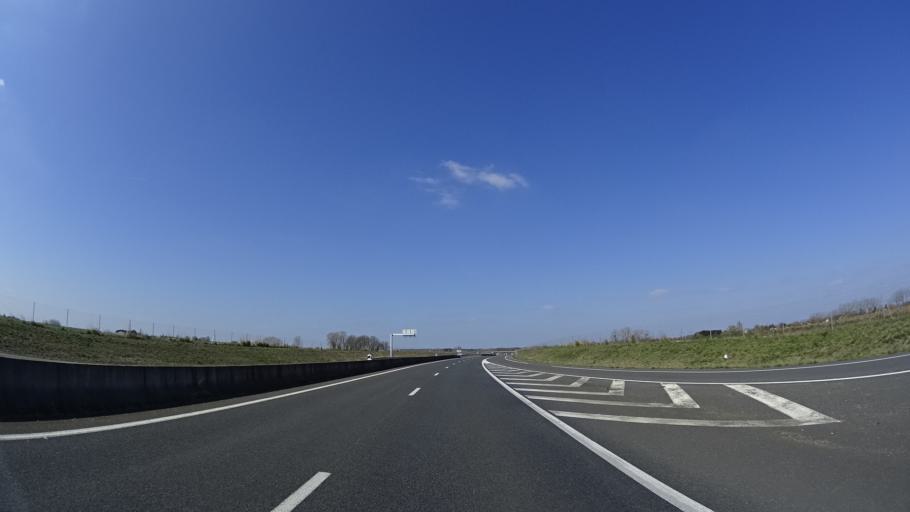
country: FR
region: Pays de la Loire
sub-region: Departement de Maine-et-Loire
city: Saint-Jean
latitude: 47.2866
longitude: -0.3749
